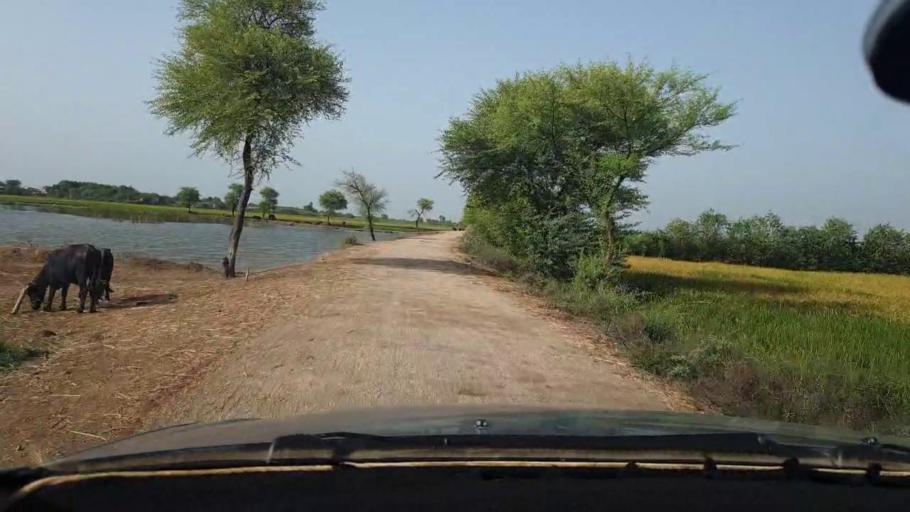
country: PK
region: Sindh
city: Tando Bago
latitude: 24.8219
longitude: 68.9007
